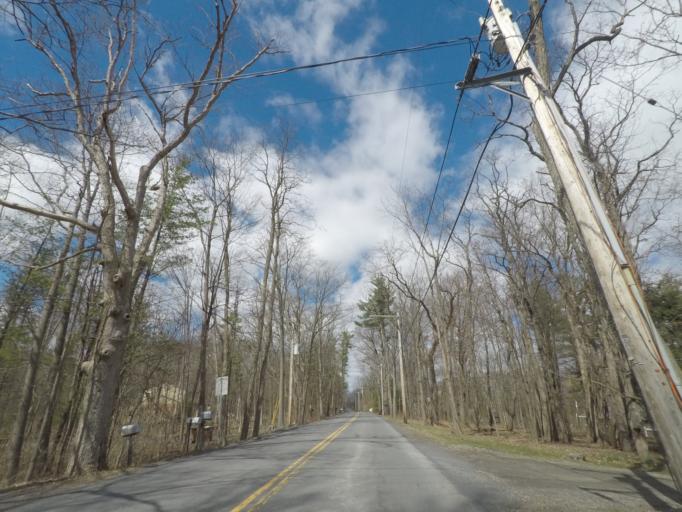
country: US
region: New York
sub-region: Albany County
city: Voorheesville
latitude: 42.6328
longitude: -73.9275
